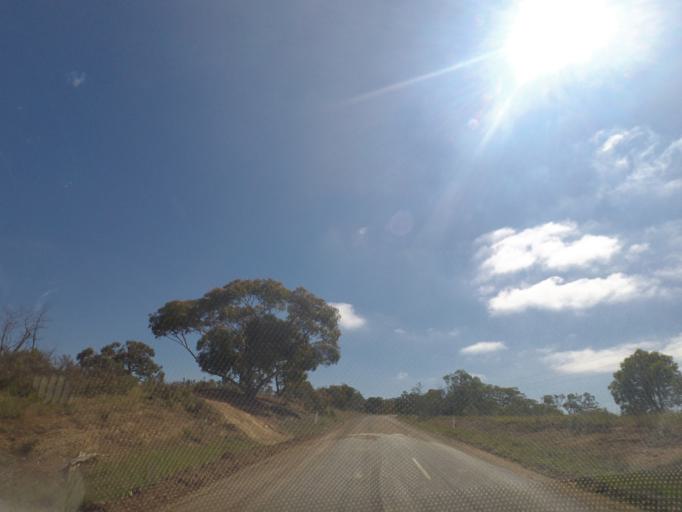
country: AU
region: Victoria
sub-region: Hume
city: Craigieburn
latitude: -37.4350
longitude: 144.9379
